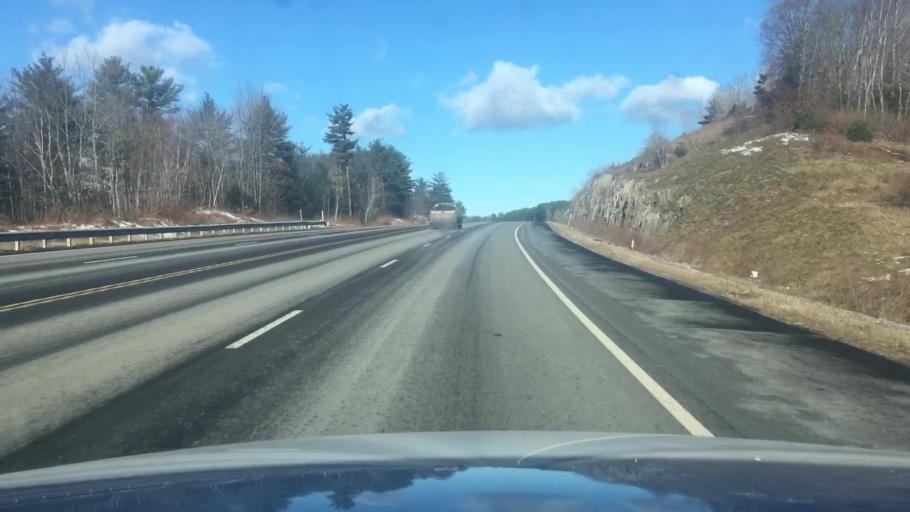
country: US
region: Maine
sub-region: Kennebec County
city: Augusta
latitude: 44.3381
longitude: -69.7668
